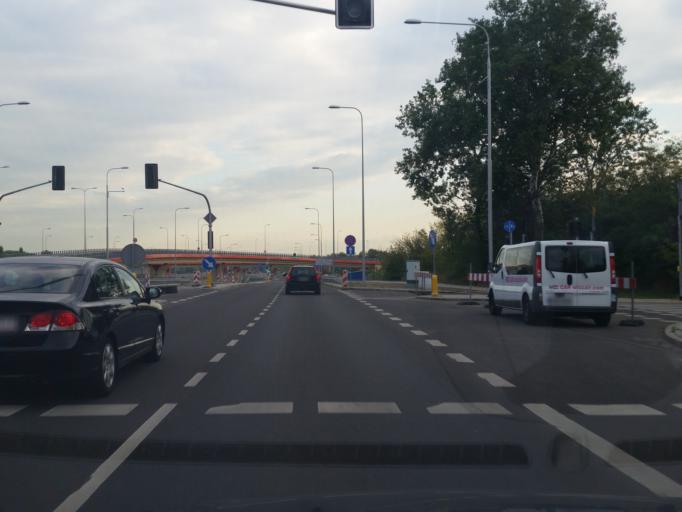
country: PL
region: Masovian Voivodeship
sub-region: Warszawa
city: Wlochy
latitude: 52.1708
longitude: 20.9853
